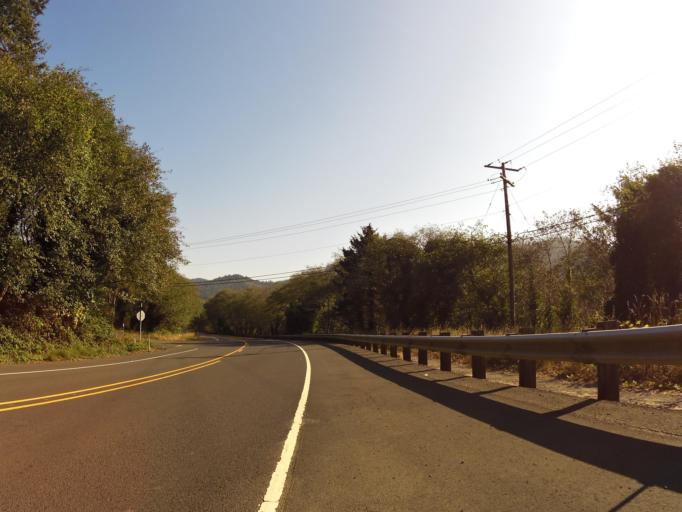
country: US
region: Oregon
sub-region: Tillamook County
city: Pacific City
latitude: 45.1009
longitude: -123.9820
